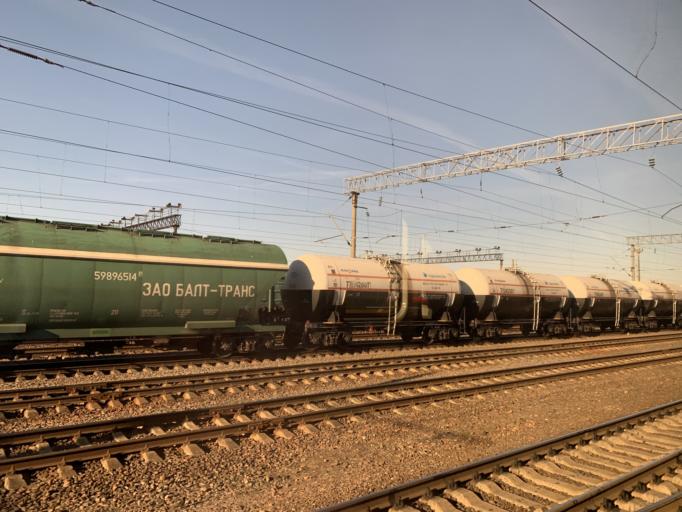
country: BY
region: Minsk
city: Maladzyechna
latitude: 54.3167
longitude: 26.8260
